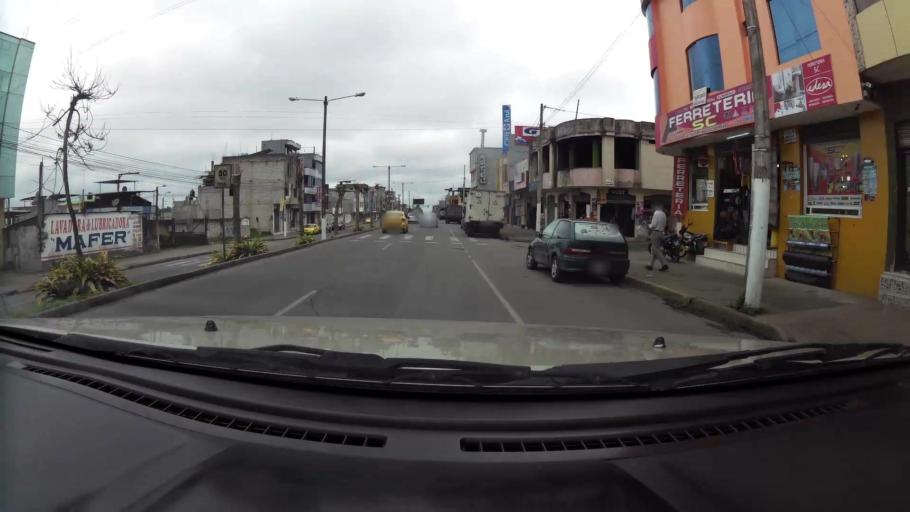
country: EC
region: Santo Domingo de los Tsachilas
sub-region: Canton Santo Domingo de los Colorados
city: Santo Domingo de los Colorados
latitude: -0.2391
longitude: -79.1735
